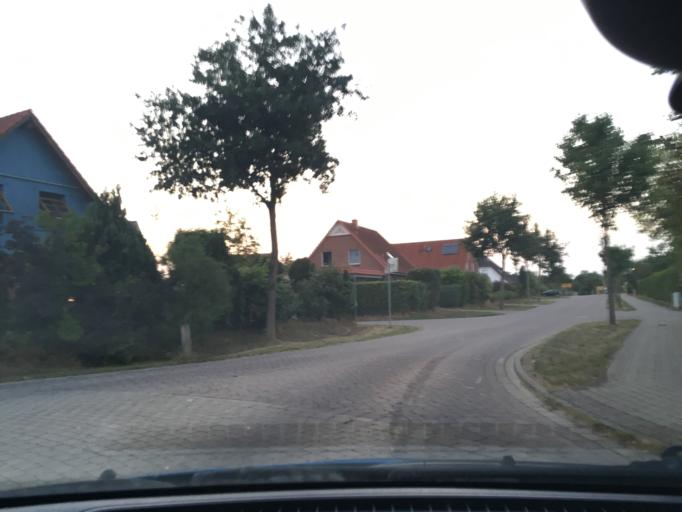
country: DE
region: Lower Saxony
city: Embsen
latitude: 53.1778
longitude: 10.3500
